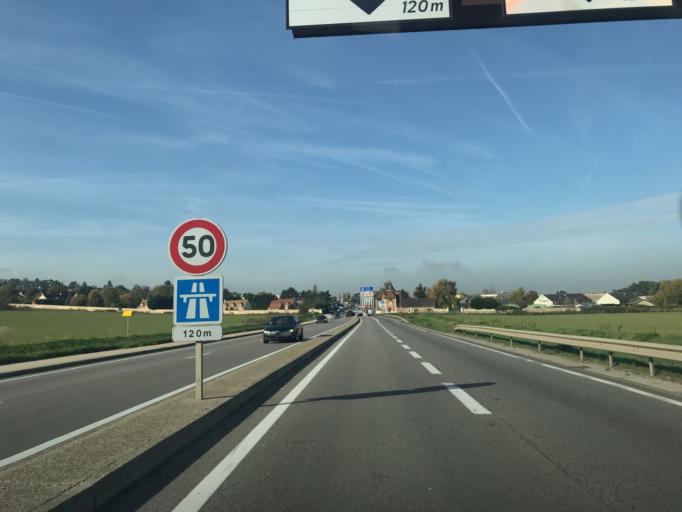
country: FR
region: Ile-de-France
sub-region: Departement des Yvelines
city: Fourqueux
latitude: 48.9027
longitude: 2.0586
